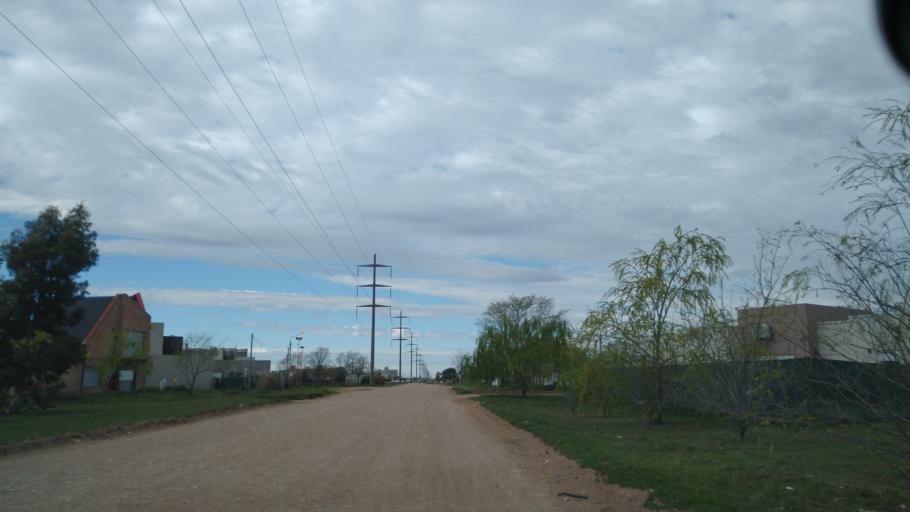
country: AR
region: Buenos Aires
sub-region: Partido de Bahia Blanca
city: Bahia Blanca
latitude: -38.7044
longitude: -62.2033
